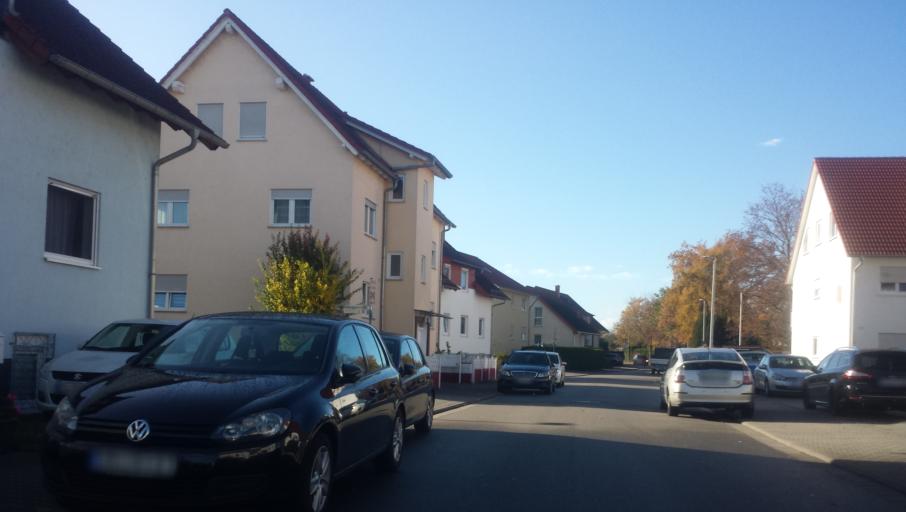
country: DE
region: Hesse
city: Gernsheim
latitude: 49.7448
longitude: 8.4892
